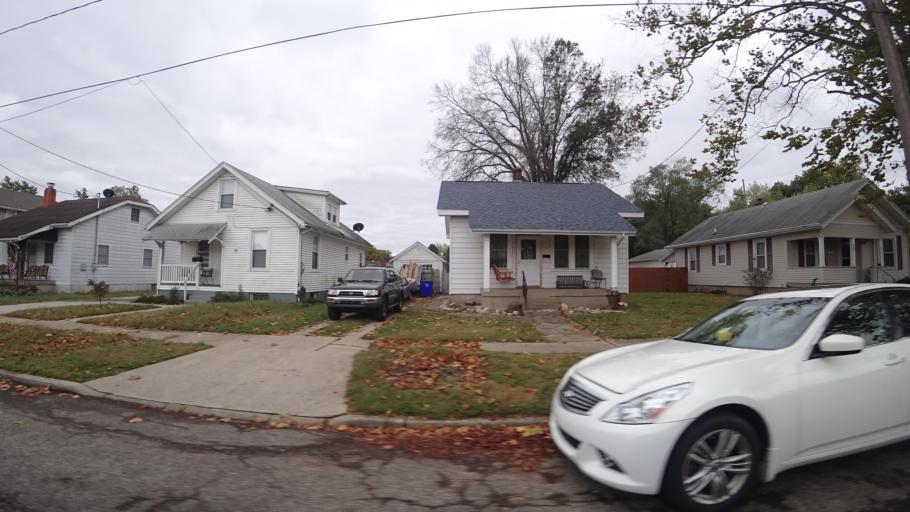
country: US
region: Ohio
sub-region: Butler County
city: Fairfield
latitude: 39.3643
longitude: -84.5621
